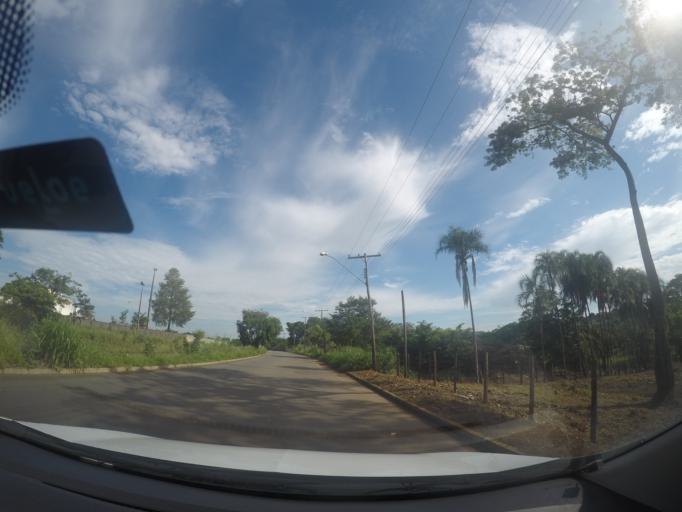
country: BR
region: Goias
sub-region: Goiania
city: Goiania
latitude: -16.6697
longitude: -49.2014
